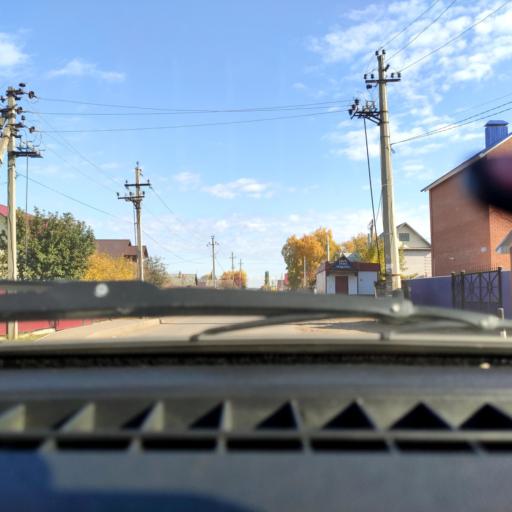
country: RU
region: Bashkortostan
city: Ufa
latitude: 54.6102
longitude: 55.9399
